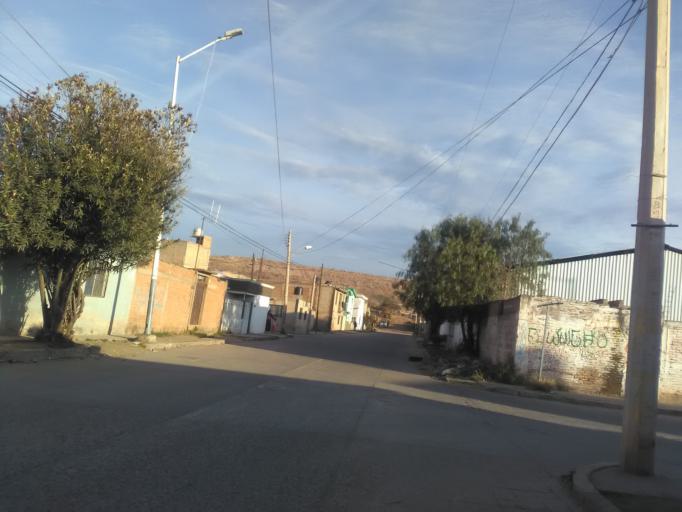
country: MX
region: Durango
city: Victoria de Durango
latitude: 24.0456
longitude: -104.6638
